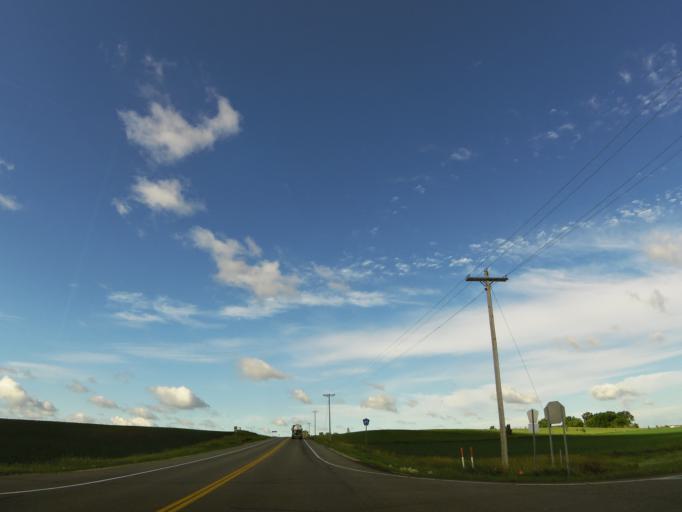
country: US
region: Minnesota
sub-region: Dakota County
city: Hastings
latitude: 44.6735
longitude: -92.9266
